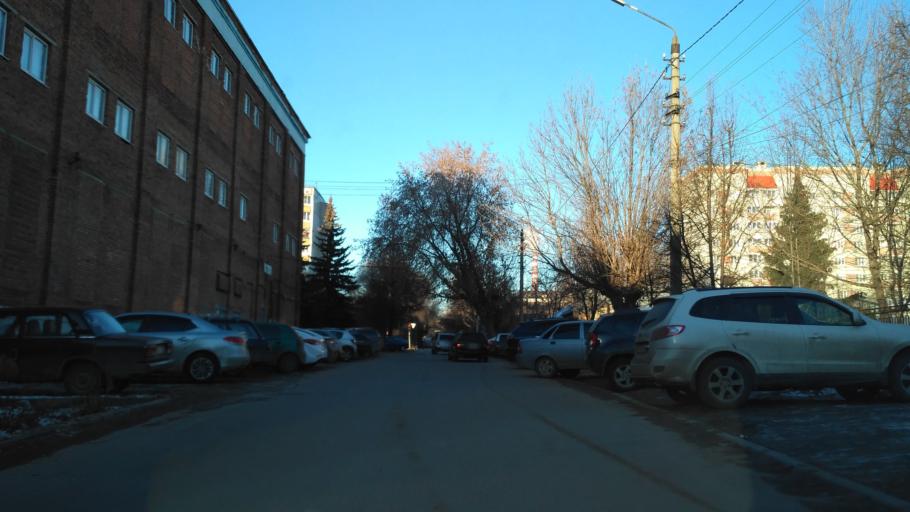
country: RU
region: Tula
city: Tula
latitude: 54.2066
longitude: 37.6079
